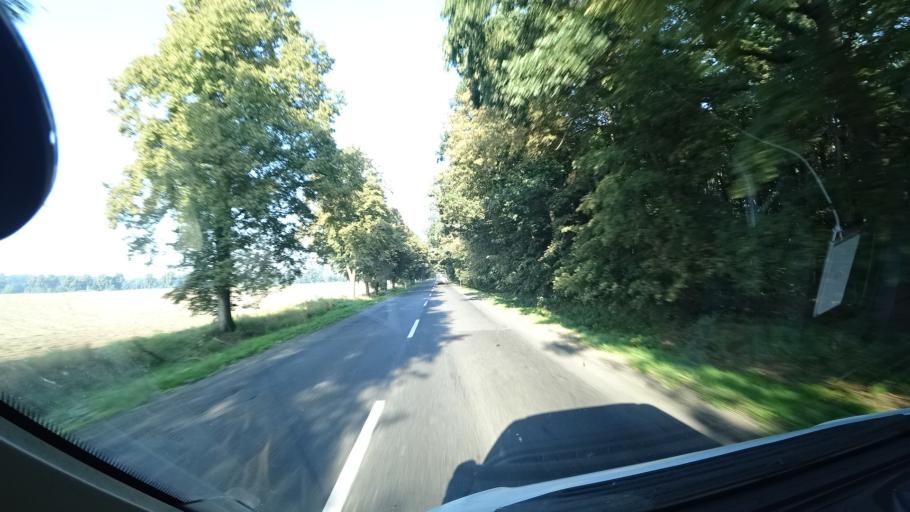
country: PL
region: Opole Voivodeship
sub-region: Powiat kedzierzynsko-kozielski
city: Bierawa
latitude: 50.2950
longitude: 18.2410
